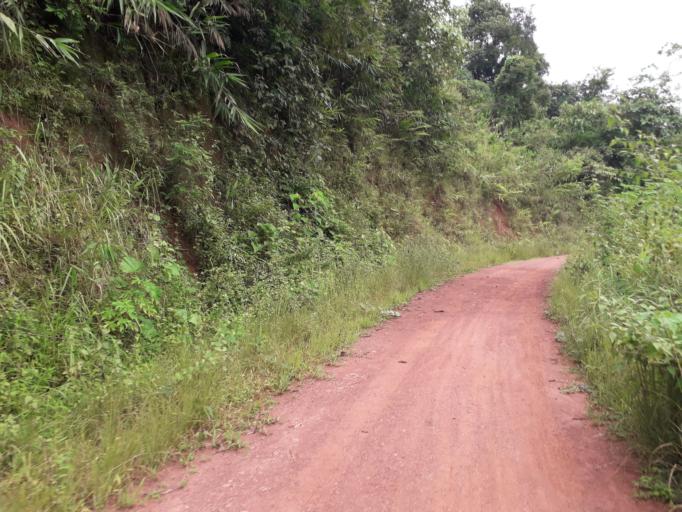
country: CN
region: Yunnan
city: Menglie
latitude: 22.2419
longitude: 101.6115
